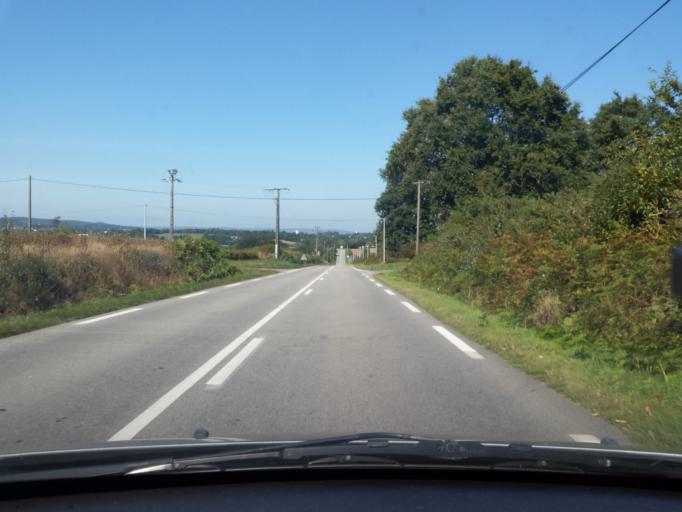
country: FR
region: Brittany
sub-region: Departement du Morbihan
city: Saint-Thuriau
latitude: 48.0482
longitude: -2.9284
